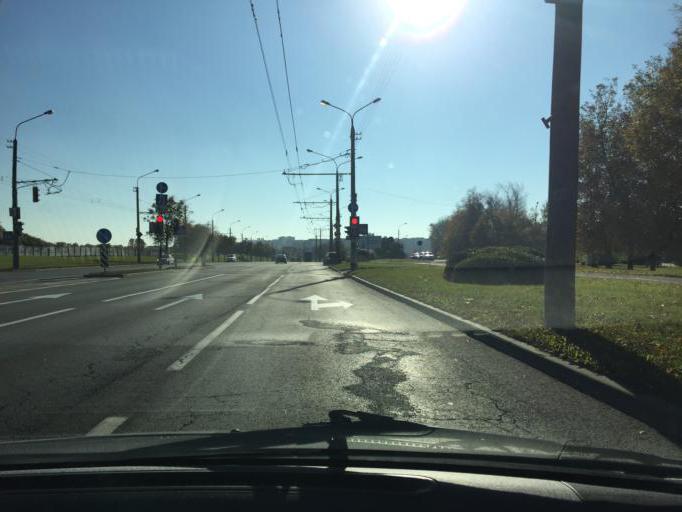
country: BY
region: Minsk
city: Syenitsa
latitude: 53.8627
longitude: 27.5335
